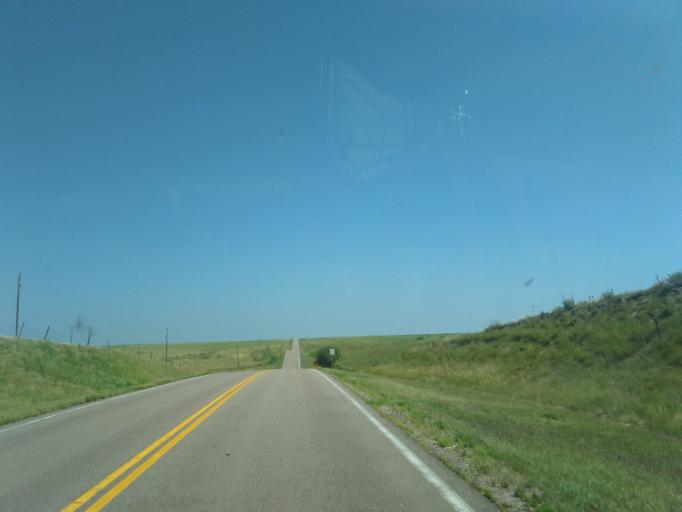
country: US
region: Nebraska
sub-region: Dundy County
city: Benkelman
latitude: 39.9406
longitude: -101.5414
